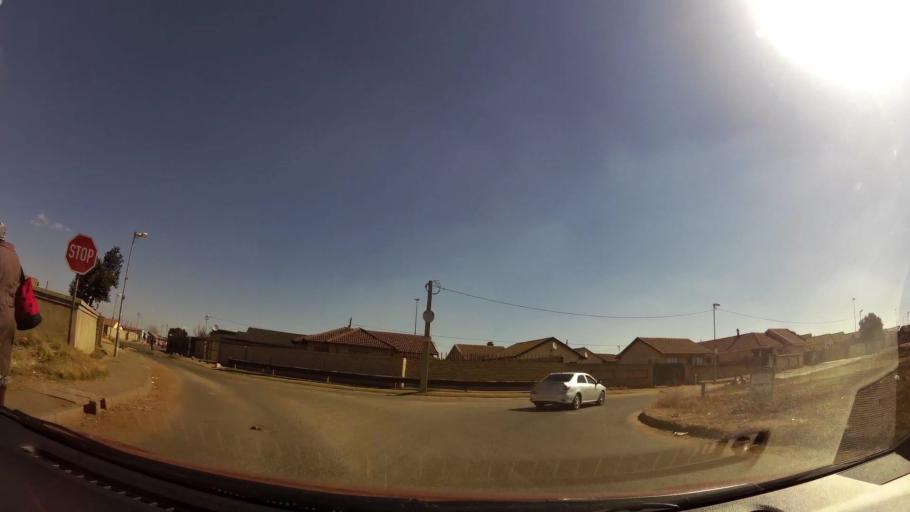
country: ZA
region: Gauteng
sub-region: City of Johannesburg Metropolitan Municipality
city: Soweto
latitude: -26.2509
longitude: 27.8080
